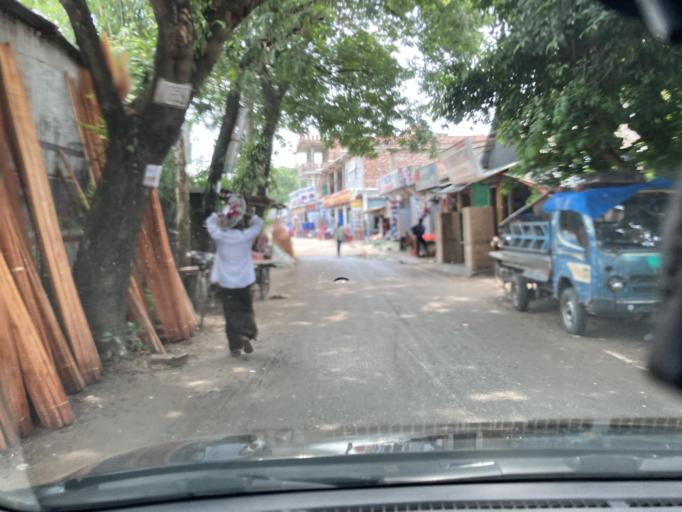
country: BD
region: Dhaka
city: Dohar
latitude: 23.7611
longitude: 90.2023
